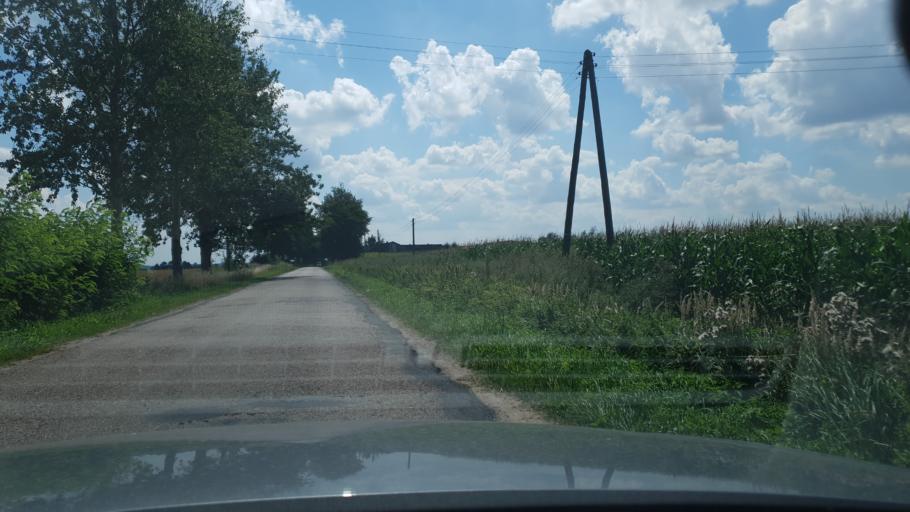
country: PL
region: Kujawsko-Pomorskie
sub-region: Powiat wabrzeski
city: Pluznica
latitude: 53.2875
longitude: 18.8309
